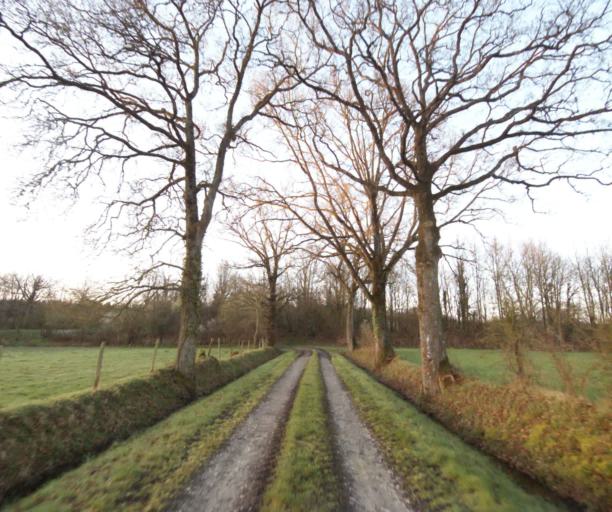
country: FR
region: Pays de la Loire
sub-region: Departement de la Loire-Atlantique
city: Campbon
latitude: 47.4192
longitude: -1.9101
